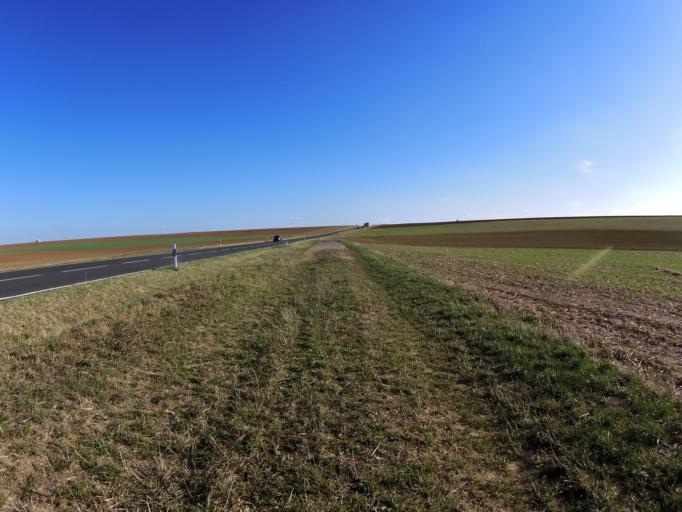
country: DE
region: Bavaria
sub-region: Regierungsbezirk Unterfranken
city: Reichenberg
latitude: 49.7200
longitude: 9.9380
